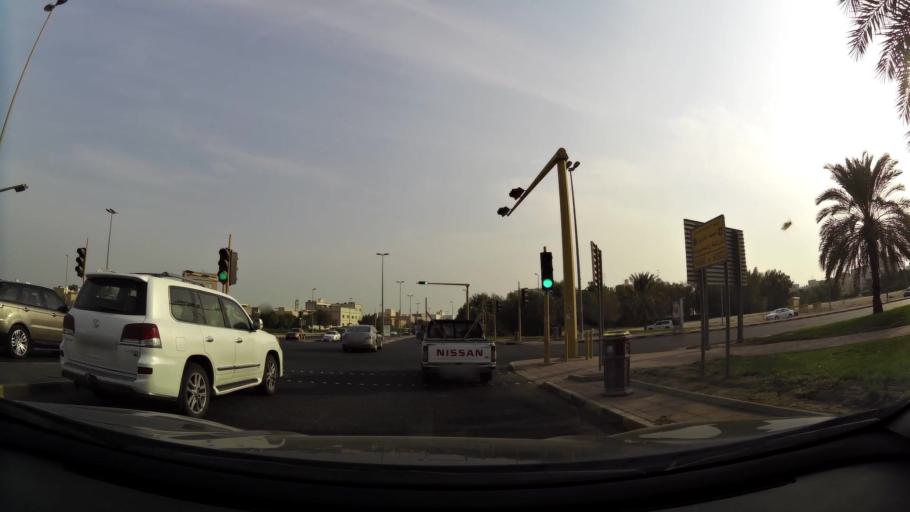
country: KW
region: Mubarak al Kabir
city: Mubarak al Kabir
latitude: 29.2085
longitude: 48.0689
